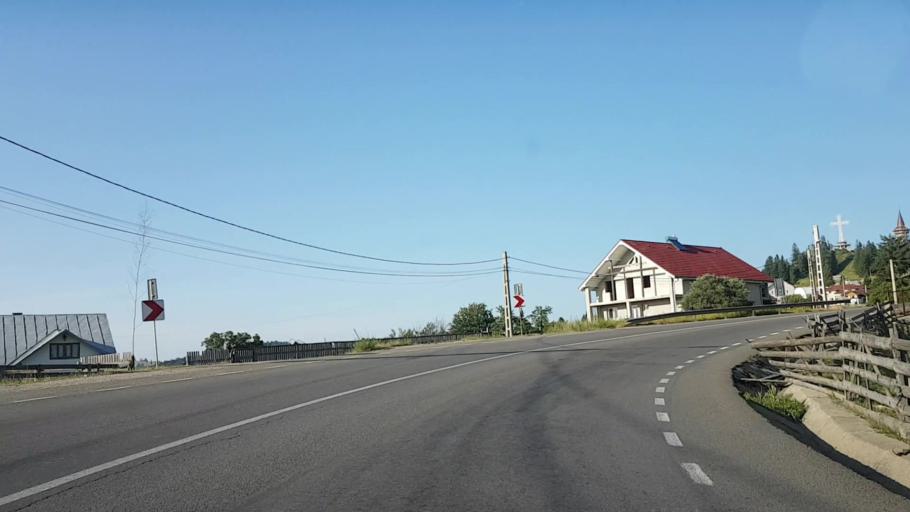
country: RO
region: Bistrita-Nasaud
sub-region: Comuna Lunca Ilvei
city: Lunca Ilvei
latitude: 47.2362
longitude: 25.0013
